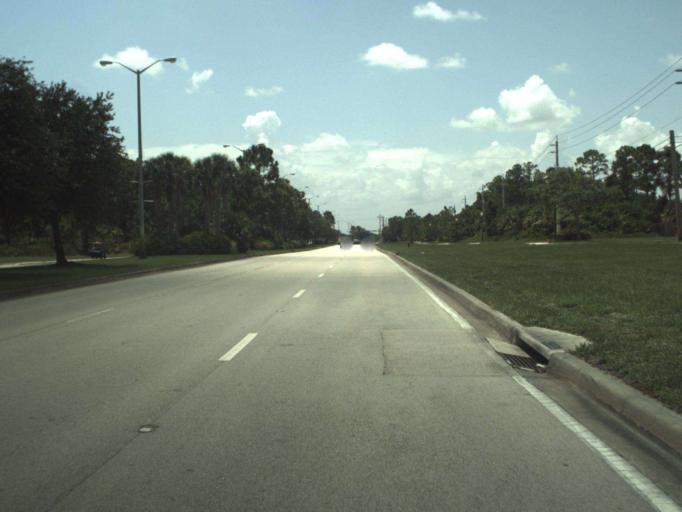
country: US
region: Florida
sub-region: Saint Lucie County
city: Port Saint Lucie
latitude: 27.2612
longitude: -80.3834
